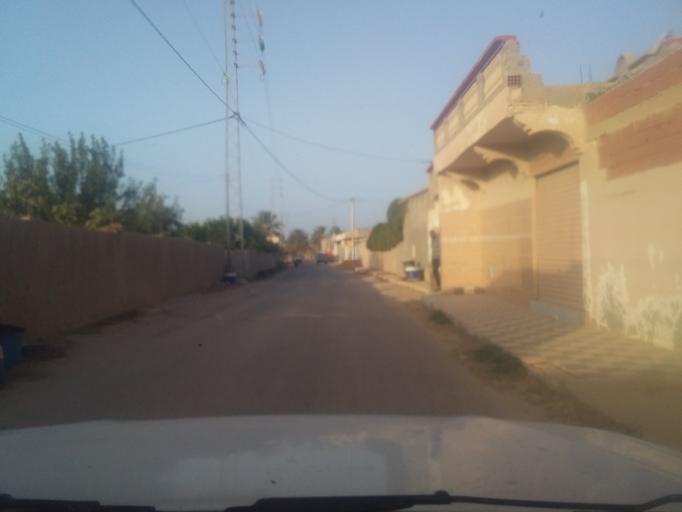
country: TN
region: Qabis
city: Gabes
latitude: 33.6220
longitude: 10.2931
